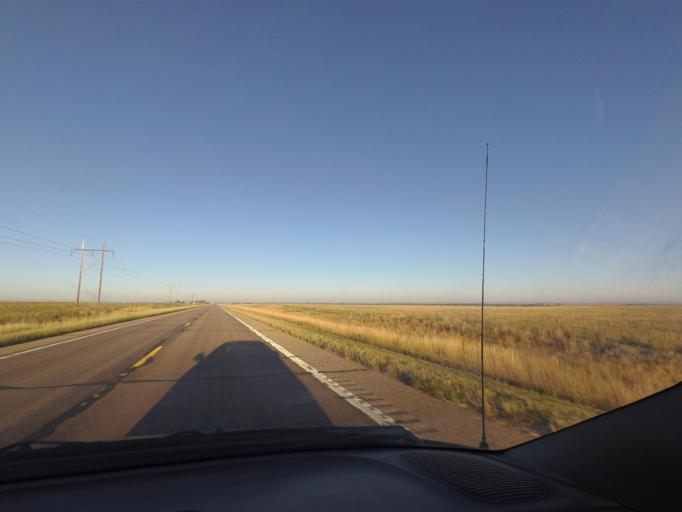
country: US
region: Colorado
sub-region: Yuma County
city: Yuma
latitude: 39.6549
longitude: -102.8079
